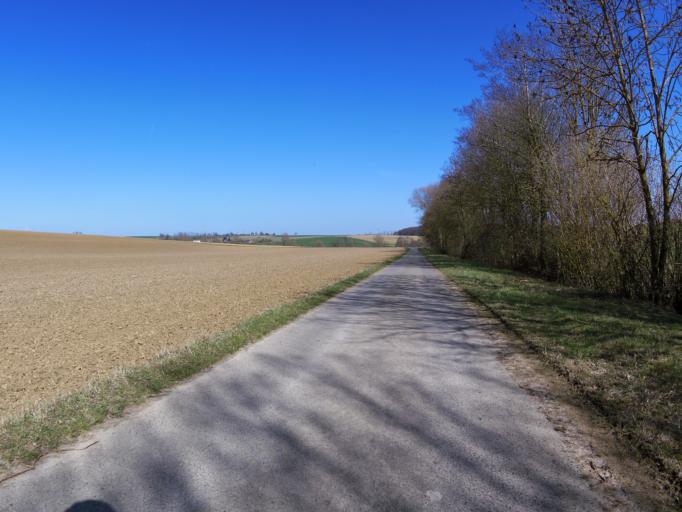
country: DE
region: Bavaria
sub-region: Regierungsbezirk Unterfranken
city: Prosselsheim
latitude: 49.8556
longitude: 10.1284
